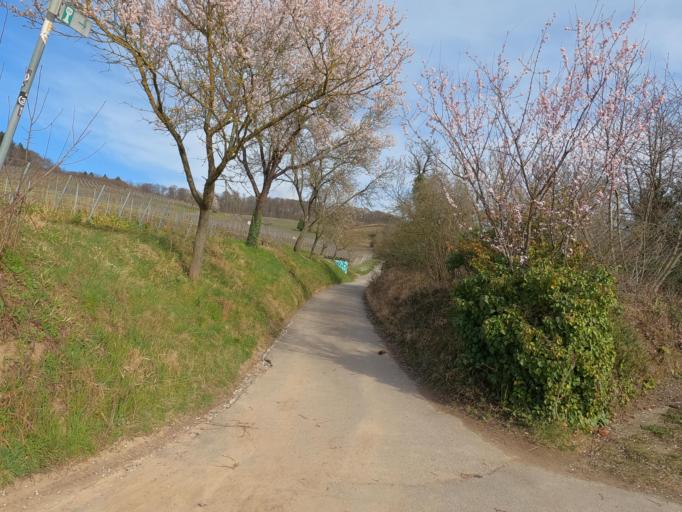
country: DE
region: Baden-Wuerttemberg
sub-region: Karlsruhe Region
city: Laudenbach
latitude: 49.6277
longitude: 8.6471
